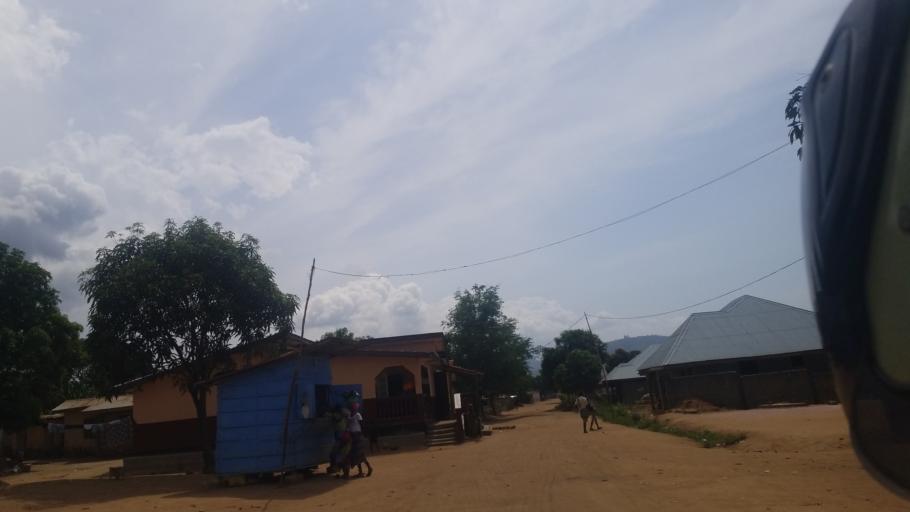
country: SL
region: Western Area
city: Waterloo
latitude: 8.3194
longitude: -13.0450
